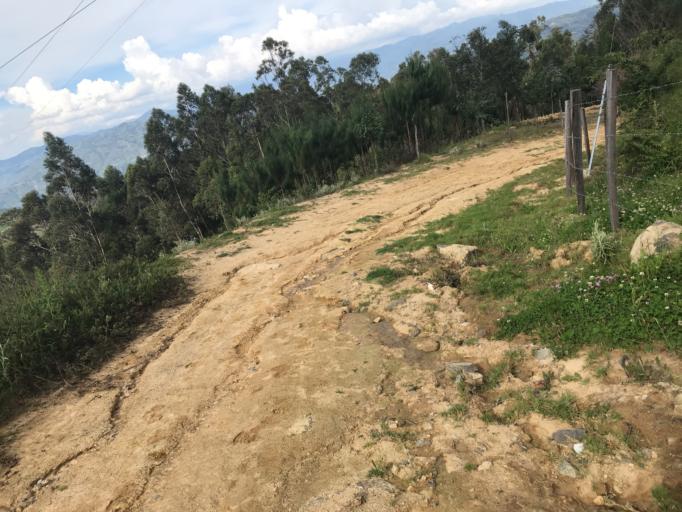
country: PE
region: Cajamarca
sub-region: Provincia de Chota
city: Querocoto
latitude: -6.3630
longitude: -79.0308
